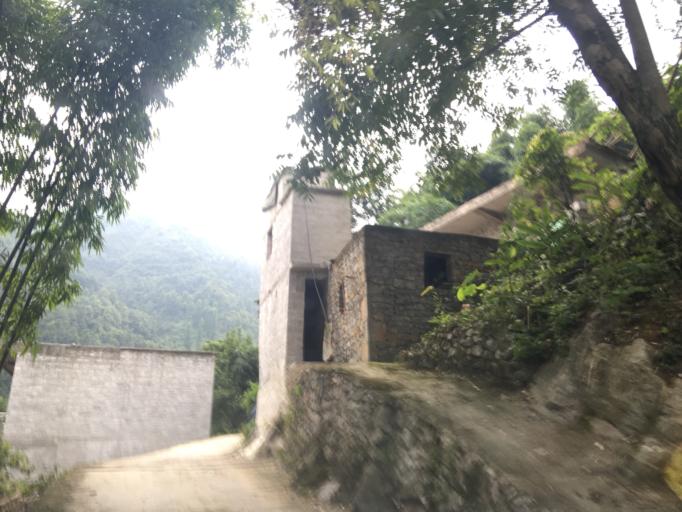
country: CN
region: Guangxi Zhuangzu Zizhiqu
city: Xinzhou
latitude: 25.0757
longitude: 105.7270
